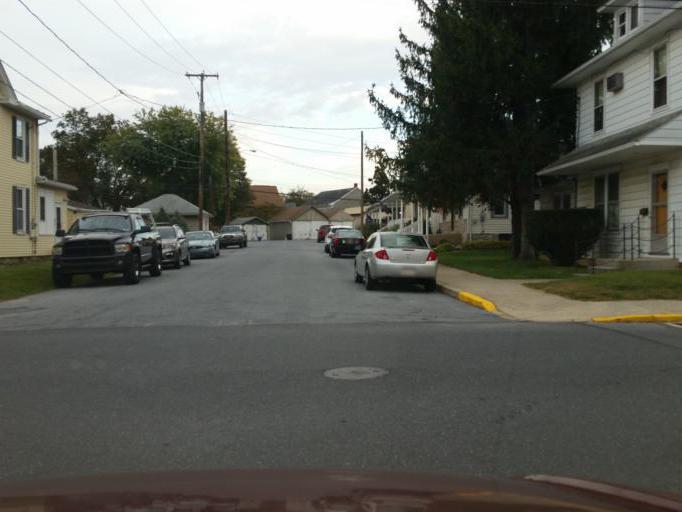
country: US
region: Pennsylvania
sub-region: Dauphin County
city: Hummelstown
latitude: 40.2639
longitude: -76.7119
